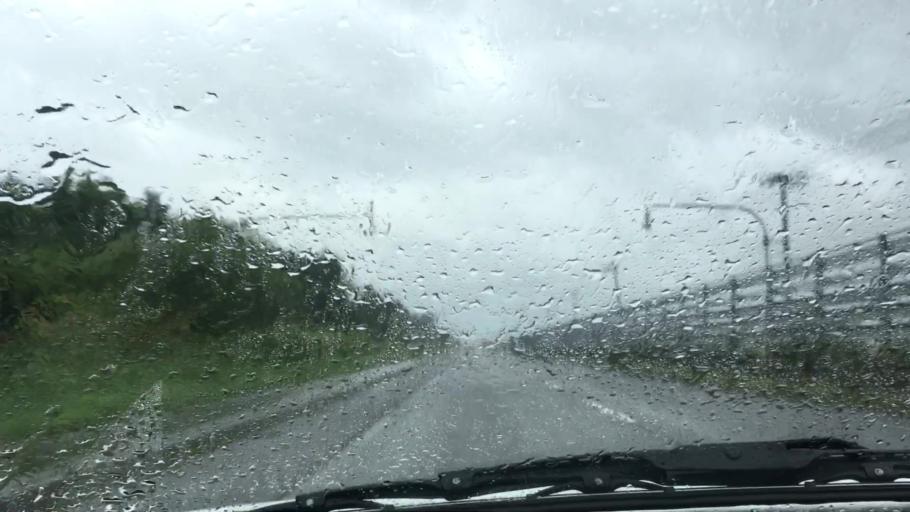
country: JP
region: Hokkaido
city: Nanae
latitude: 42.3106
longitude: 140.2731
